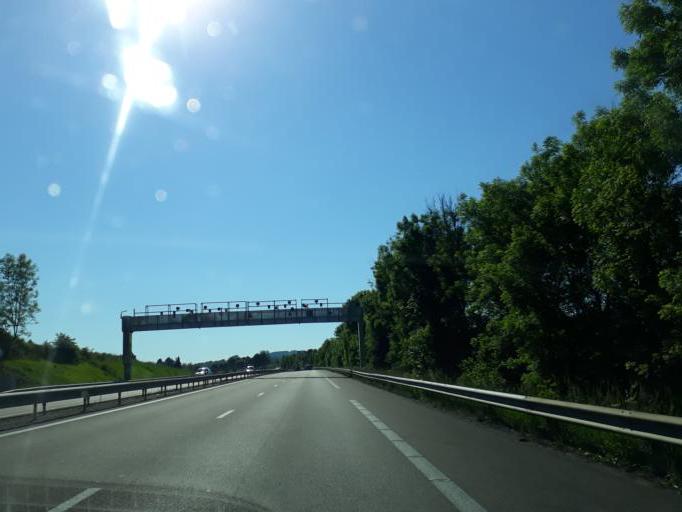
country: FR
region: Bourgogne
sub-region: Departement de la Cote-d'Or
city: Velars-sur-Ouche
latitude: 47.3189
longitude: 4.9233
